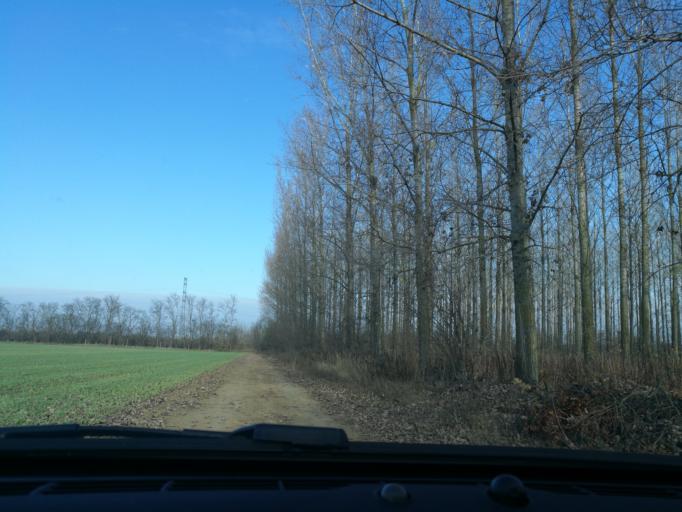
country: HU
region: Szabolcs-Szatmar-Bereg
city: Nyirpazony
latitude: 47.9577
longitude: 21.7694
